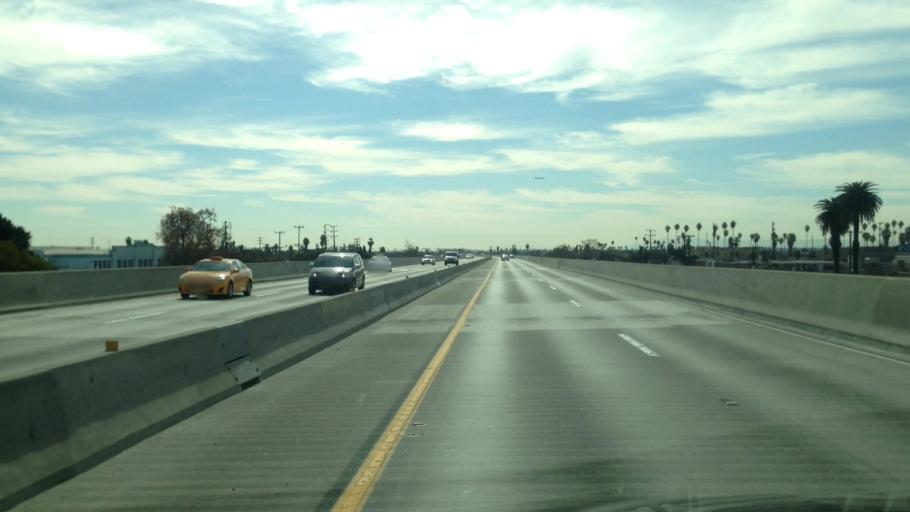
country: US
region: California
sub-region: Los Angeles County
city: Florence-Graham
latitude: 34.0068
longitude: -118.2811
